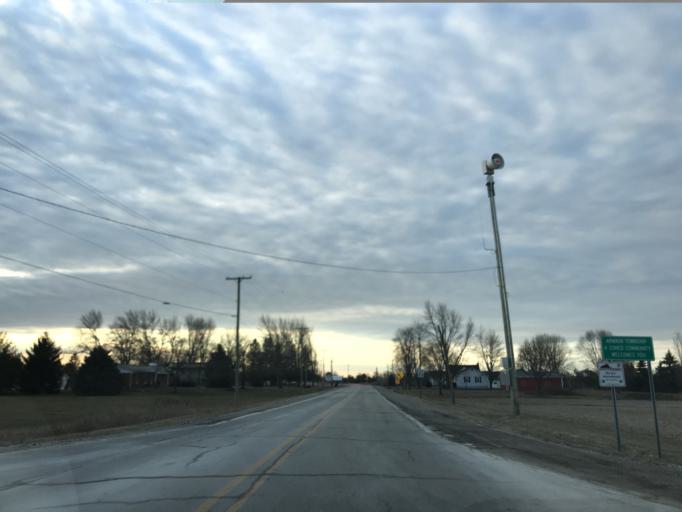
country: US
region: Michigan
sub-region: Macomb County
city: Armada
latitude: 42.8955
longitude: -82.8828
